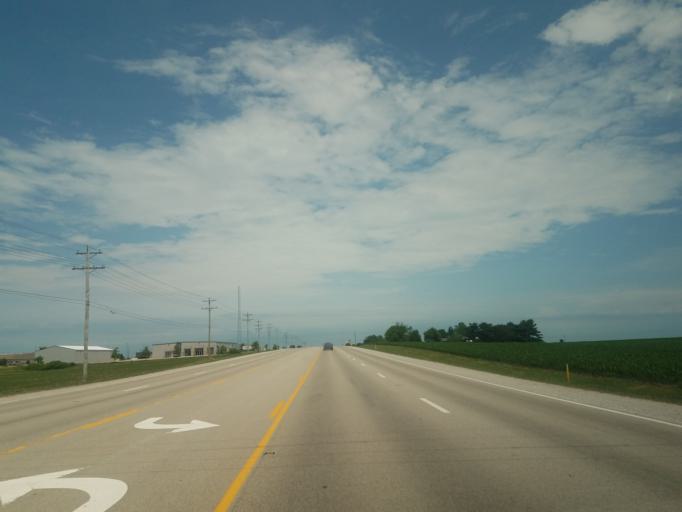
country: US
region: Illinois
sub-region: McLean County
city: Downs
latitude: 40.4656
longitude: -88.9020
